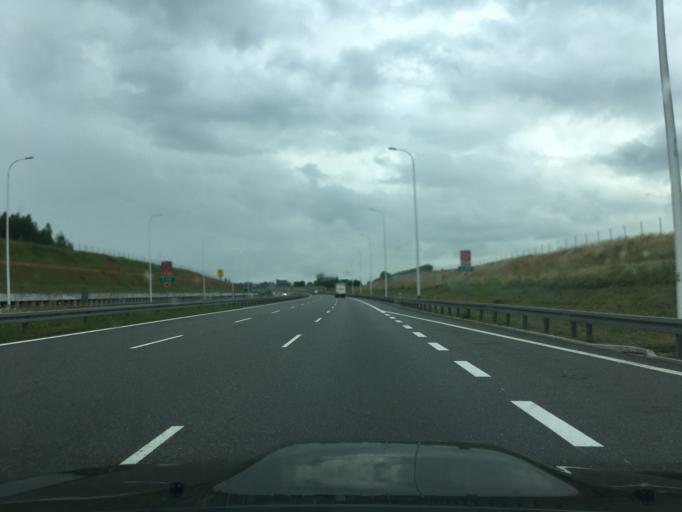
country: PL
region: Lublin Voivodeship
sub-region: Powiat lubelski
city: Lublin
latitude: 51.3012
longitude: 22.5120
